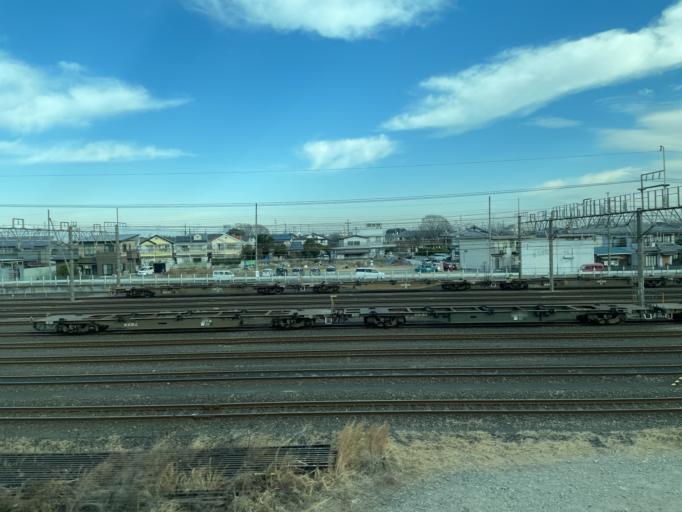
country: JP
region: Saitama
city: Kumagaya
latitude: 36.1584
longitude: 139.3600
